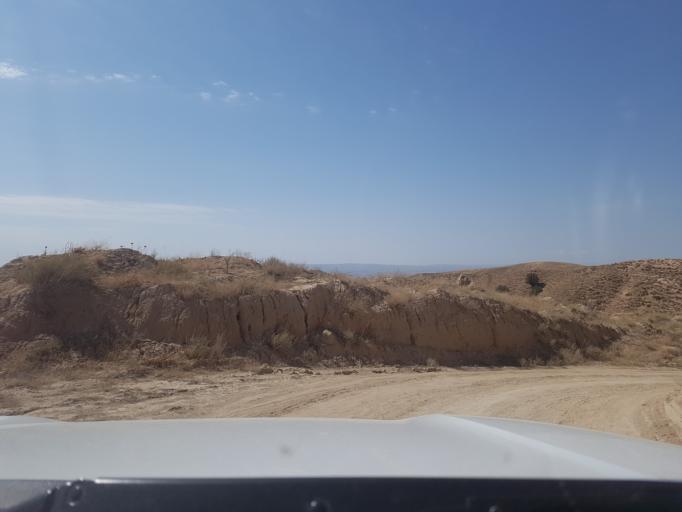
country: TM
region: Ahal
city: Baharly
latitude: 38.2773
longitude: 56.9168
